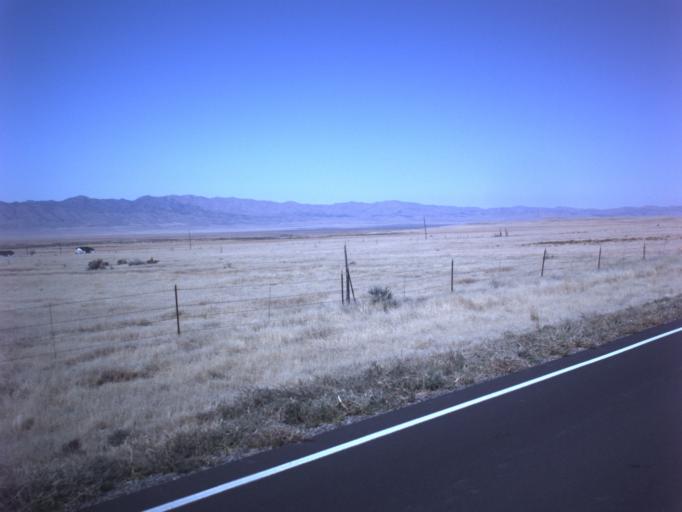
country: US
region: Utah
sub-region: Tooele County
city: Grantsville
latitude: 40.3942
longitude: -112.7476
